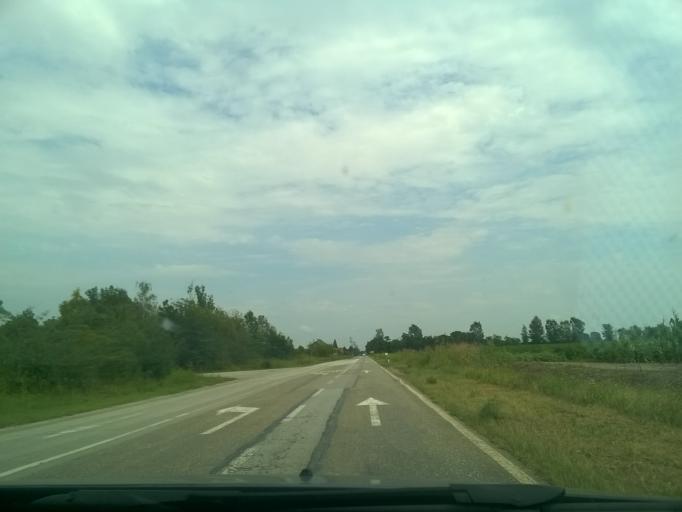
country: RS
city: Velika Greda
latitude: 45.2346
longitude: 21.0157
